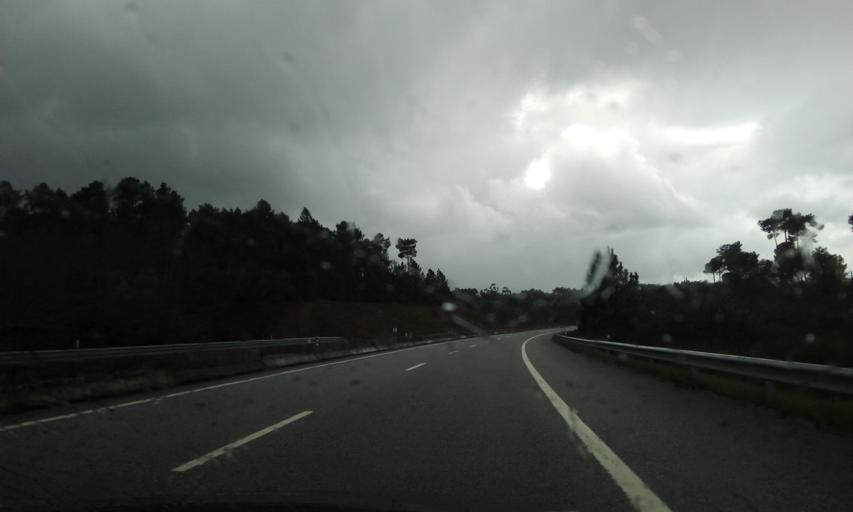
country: PT
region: Viseu
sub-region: Viseu
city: Viseu
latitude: 40.6301
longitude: -7.8890
